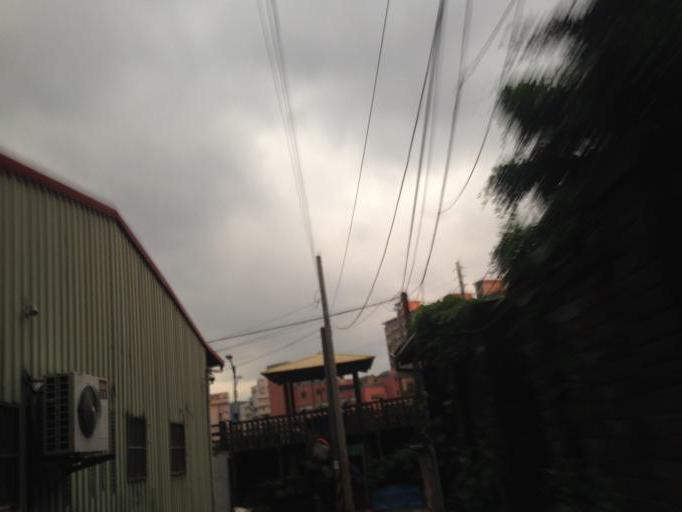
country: TW
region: Taiwan
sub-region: Taoyuan
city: Taoyuan
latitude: 24.9357
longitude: 121.3761
